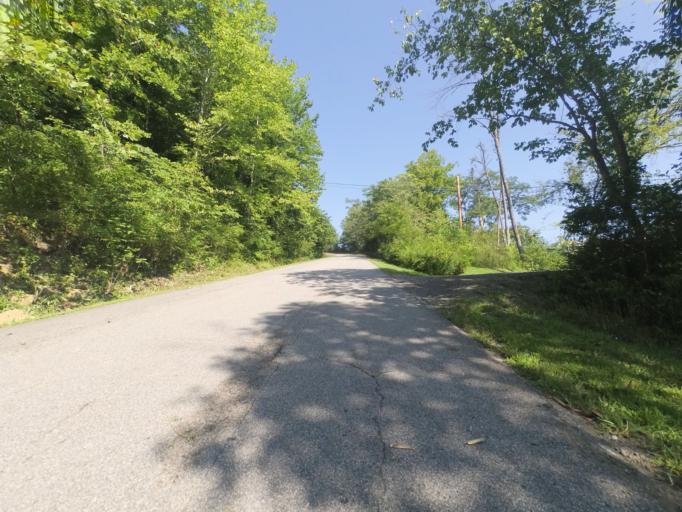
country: US
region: West Virginia
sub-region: Cabell County
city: Huntington
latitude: 38.3958
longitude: -82.4687
